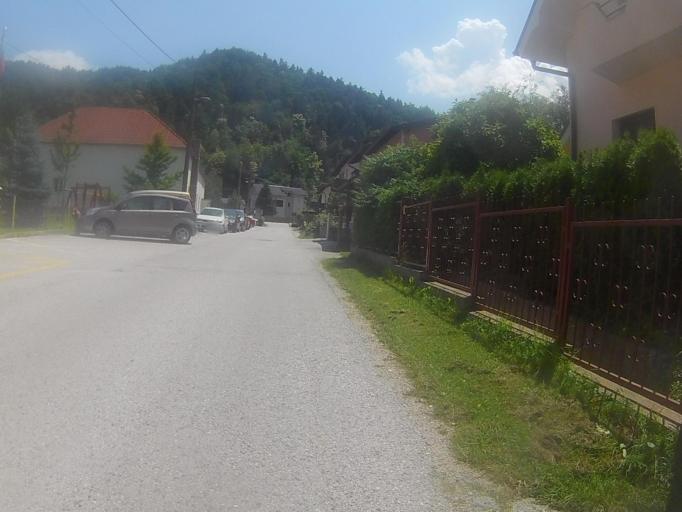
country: SI
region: Ruse
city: Bistrica ob Dravi
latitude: 46.5566
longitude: 15.5545
